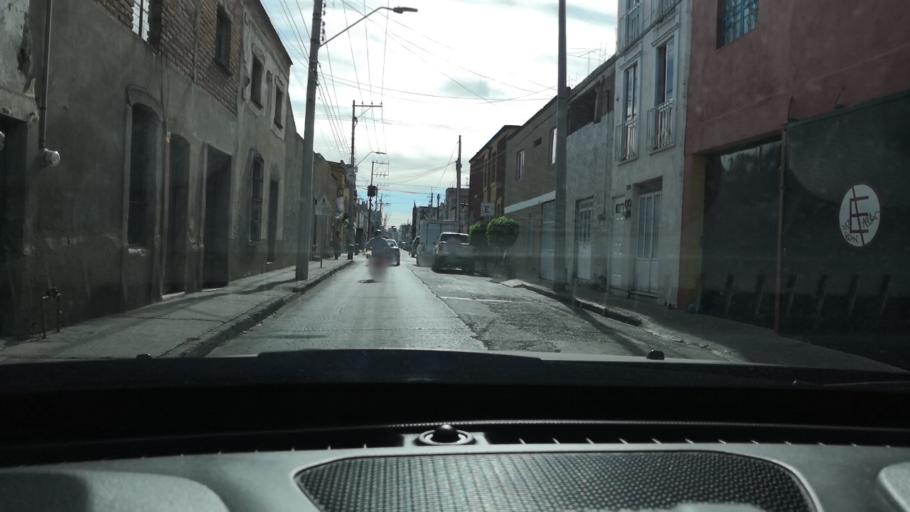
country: MX
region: Guanajuato
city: Leon
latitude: 21.1300
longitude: -101.6839
